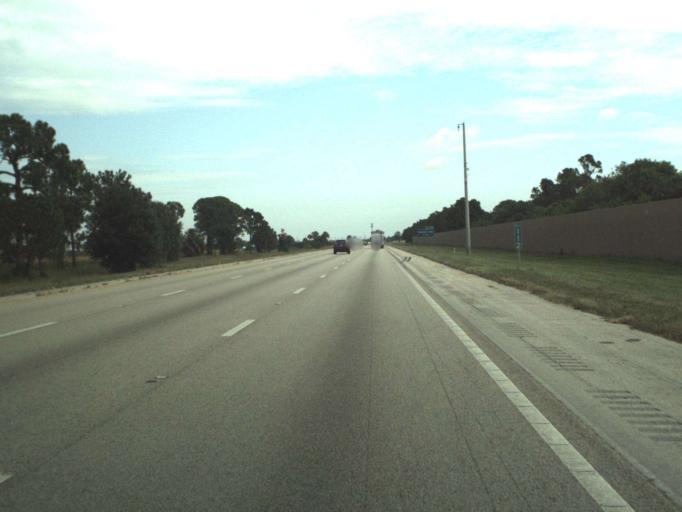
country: US
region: Florida
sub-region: Saint Lucie County
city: Port Saint Lucie
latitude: 27.1860
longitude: -80.3979
